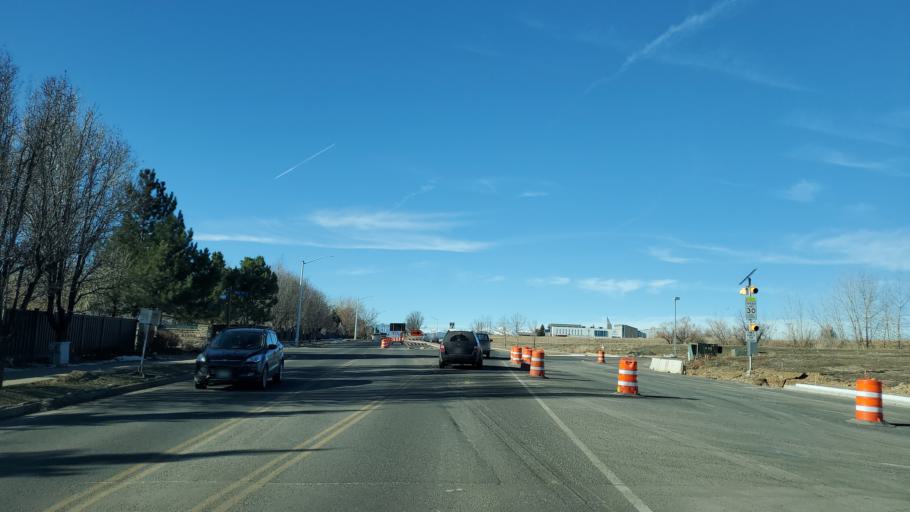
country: US
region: Colorado
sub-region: Broomfield County
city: Broomfield
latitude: 39.9577
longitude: -105.0432
